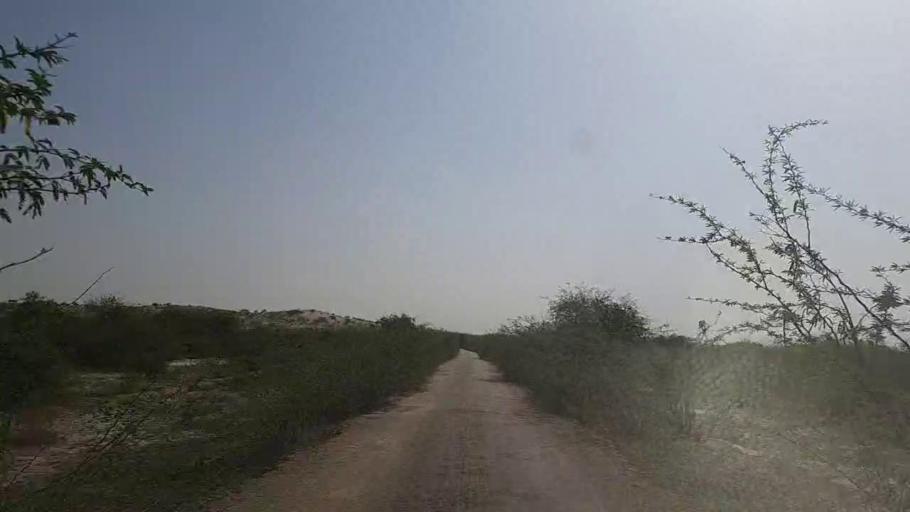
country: PK
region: Sindh
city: Naukot
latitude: 24.5736
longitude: 69.2932
